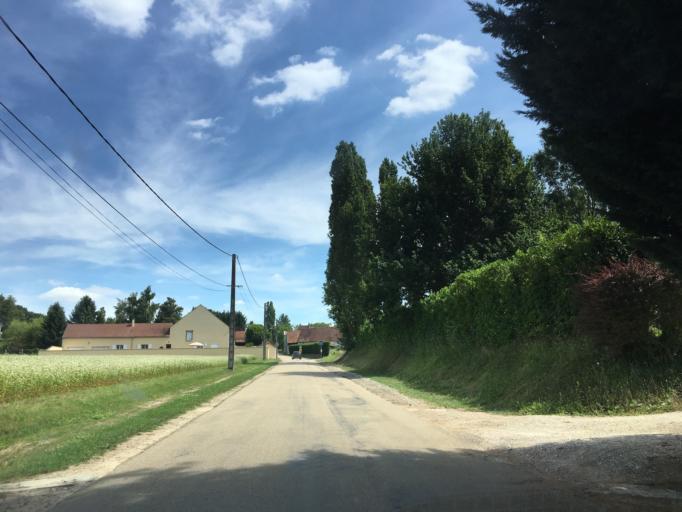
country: FR
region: Bourgogne
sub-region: Departement de l'Yonne
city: Fleury-la-Vallee
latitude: 47.8611
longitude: 3.4427
